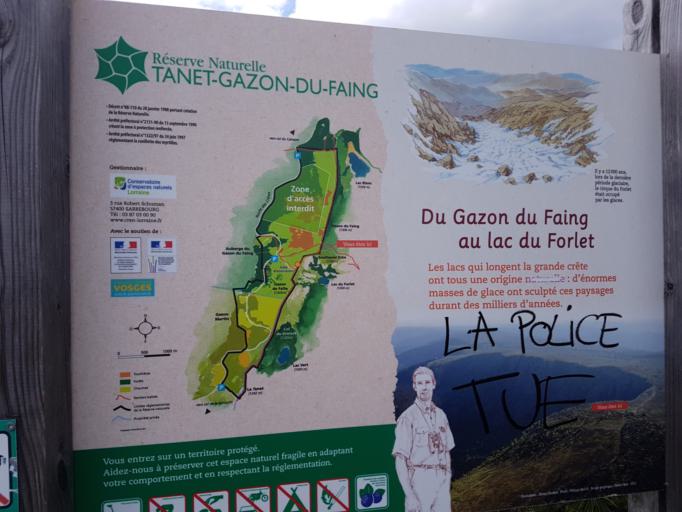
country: FR
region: Alsace
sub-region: Departement du Haut-Rhin
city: Soultzeren
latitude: 48.1086
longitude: 7.0770
